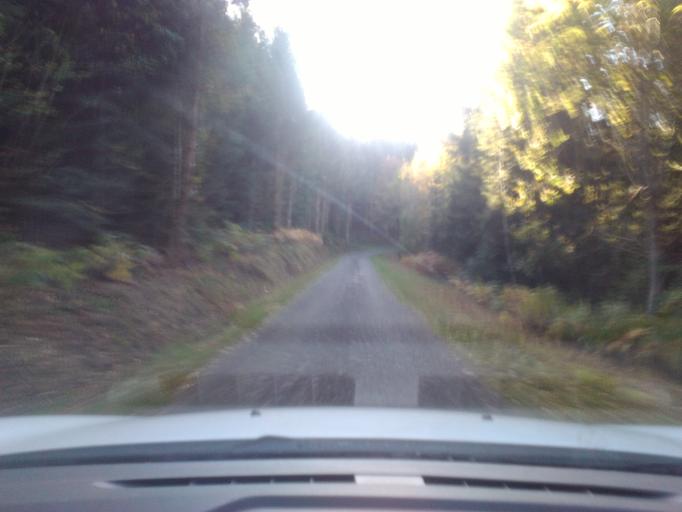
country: FR
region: Lorraine
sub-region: Departement des Vosges
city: Jeanmenil
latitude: 48.2827
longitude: 6.7287
